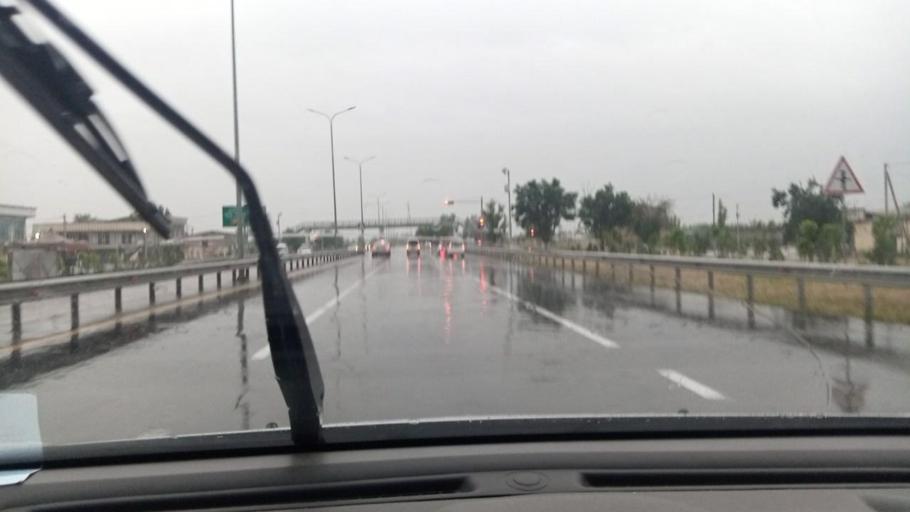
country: UZ
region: Toshkent
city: Tuytepa
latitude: 41.1319
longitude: 69.4358
